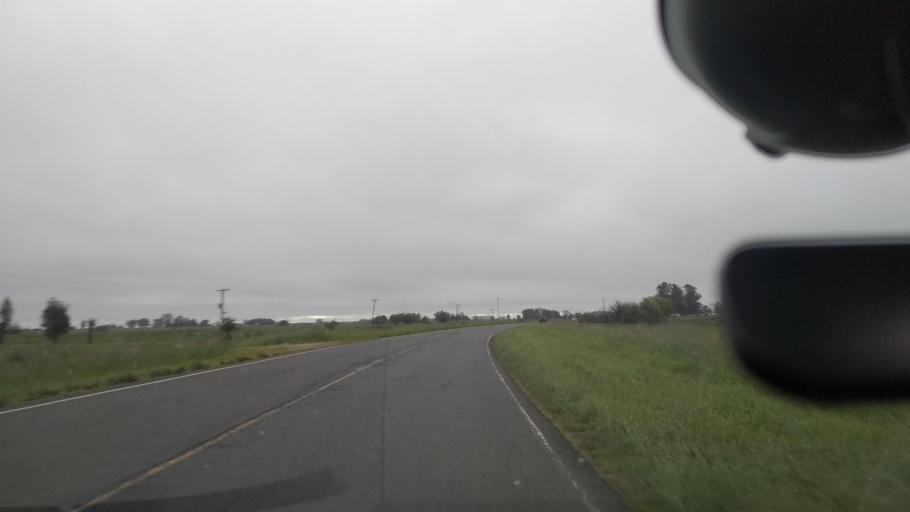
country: AR
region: Buenos Aires
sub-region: Partido de Magdalena
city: Magdalena
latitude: -35.2254
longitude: -57.7294
